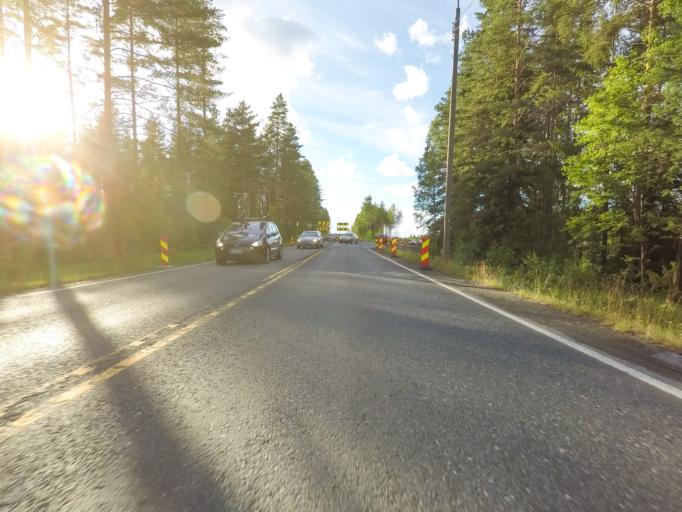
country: FI
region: Northern Savo
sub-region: Kuopio
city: Kuopio
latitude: 62.9653
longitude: 27.8478
